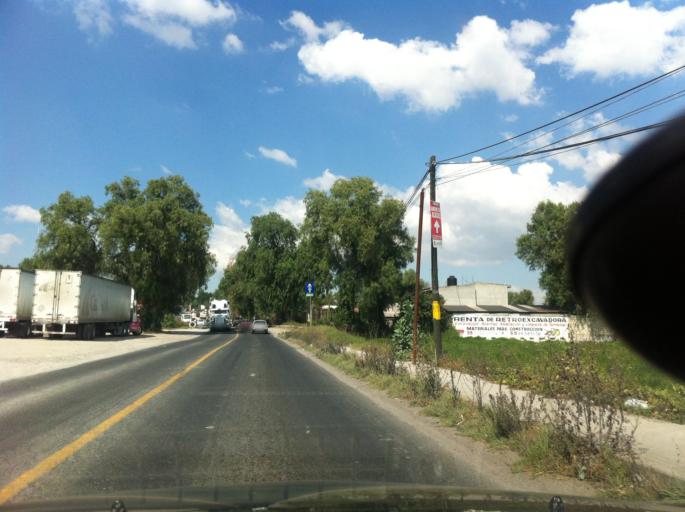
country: MX
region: Mexico
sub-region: Tequixquiac
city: Colonia Wenceslao Labra
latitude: 19.8209
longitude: -99.1152
